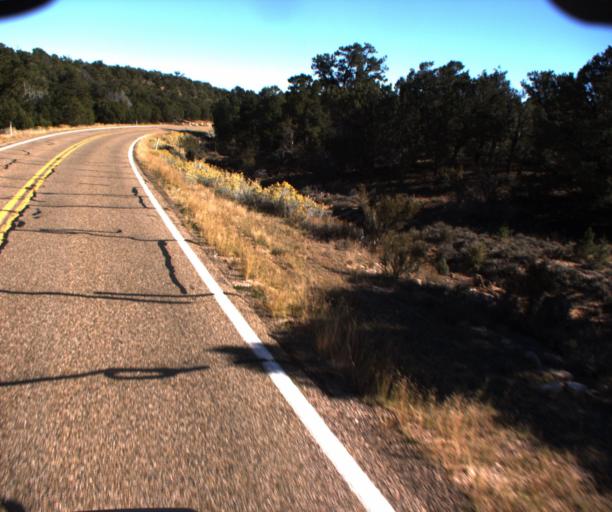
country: US
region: Arizona
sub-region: Coconino County
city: Fredonia
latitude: 36.7422
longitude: -112.1097
